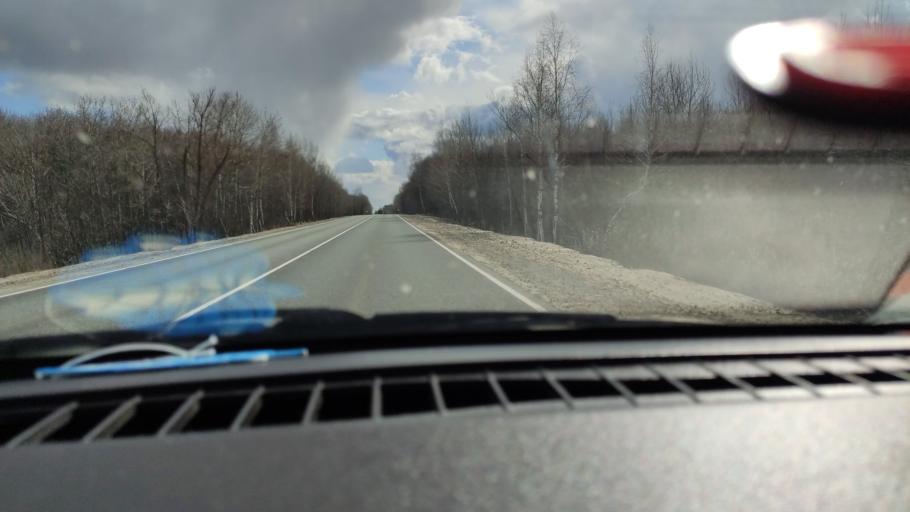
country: RU
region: Saratov
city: Khvalynsk
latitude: 52.4505
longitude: 48.0119
